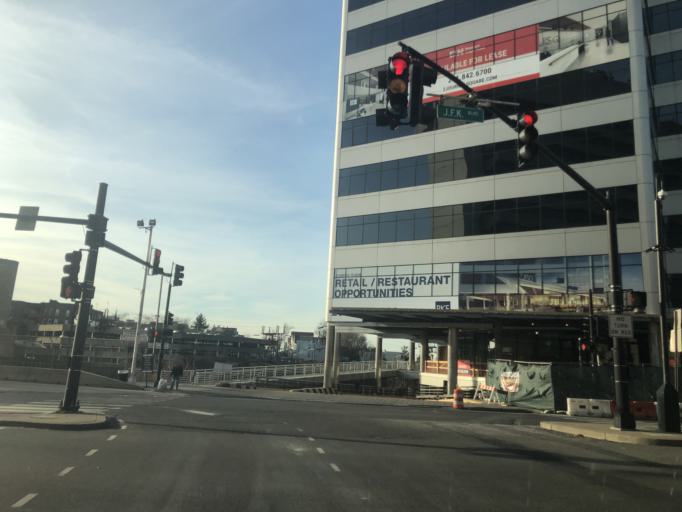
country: US
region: New Jersey
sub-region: Hudson County
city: Jersey City
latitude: 40.7331
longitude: -74.0627
